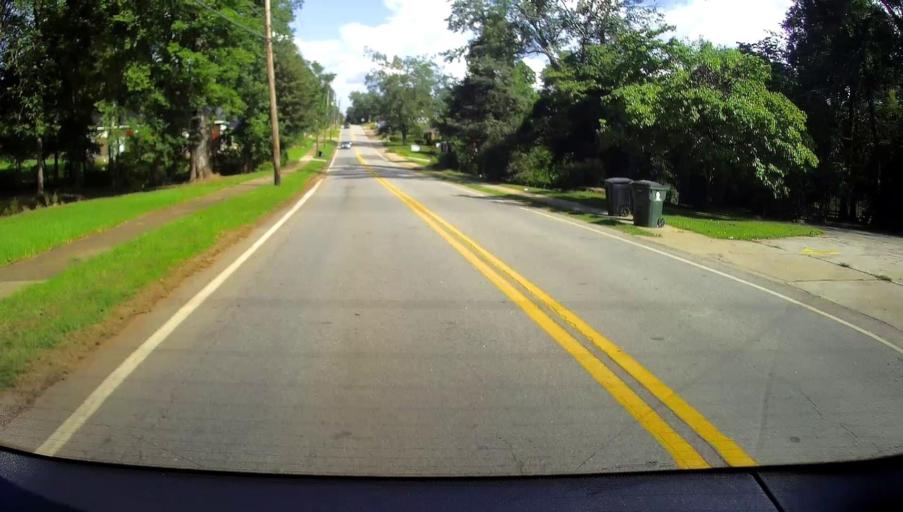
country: US
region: Georgia
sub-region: Upson County
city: Thomaston
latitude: 32.8899
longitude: -84.3330
